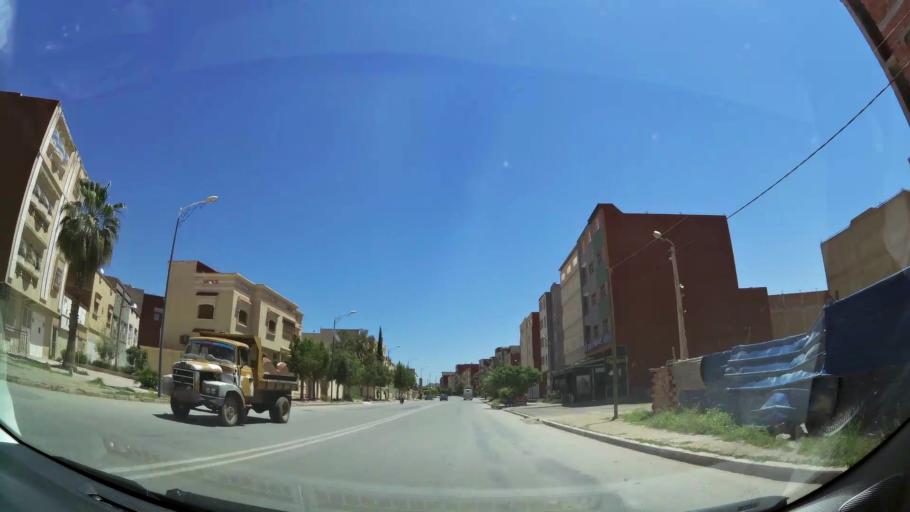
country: MA
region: Oriental
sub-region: Oujda-Angad
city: Oujda
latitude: 34.6762
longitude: -1.8803
